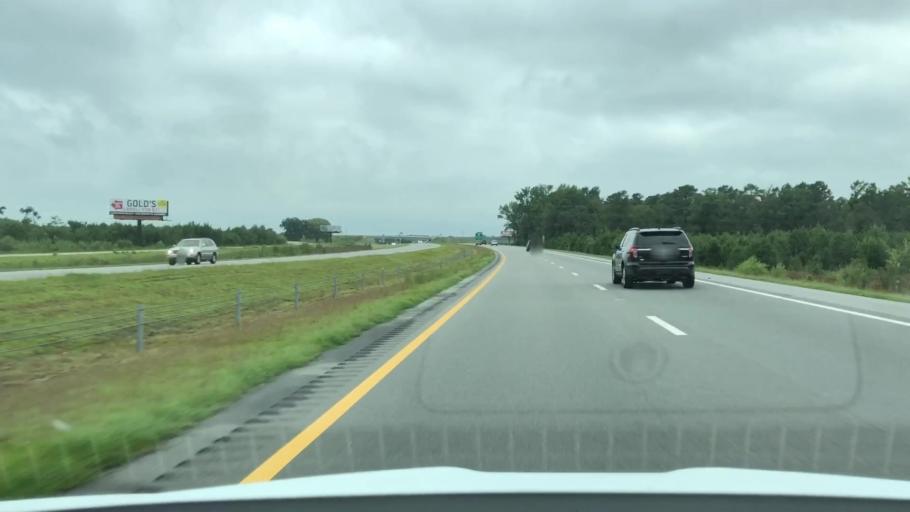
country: US
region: North Carolina
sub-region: Wayne County
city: Elroy
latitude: 35.4000
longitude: -77.8723
